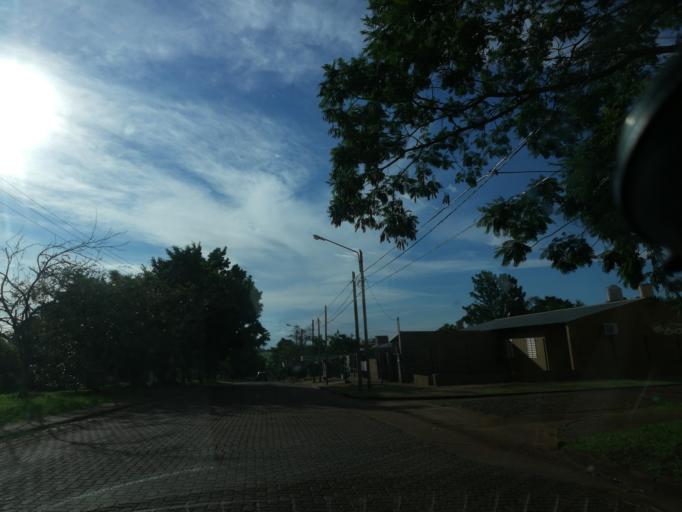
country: AR
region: Misiones
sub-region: Departamento de Capital
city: Posadas
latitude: -27.4156
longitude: -55.9518
